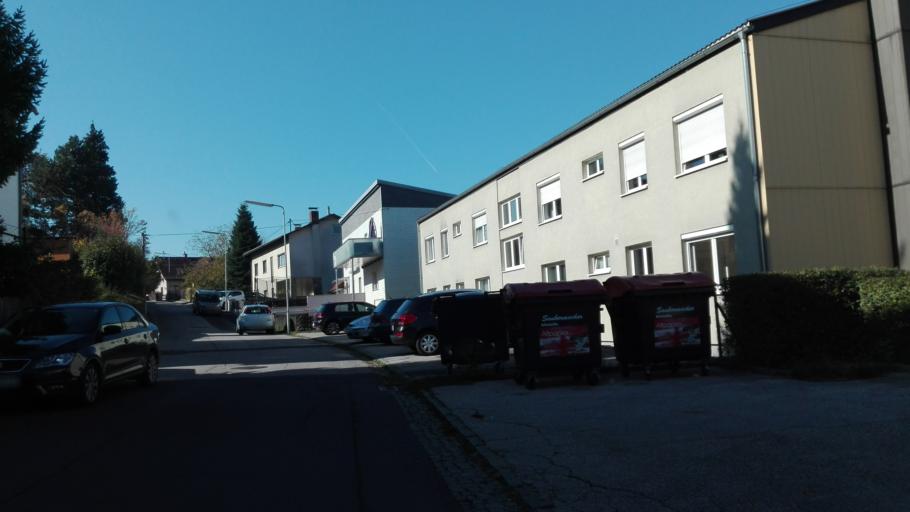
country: AT
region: Upper Austria
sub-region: Politischer Bezirk Linz-Land
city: Leonding
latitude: 48.2833
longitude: 14.2722
